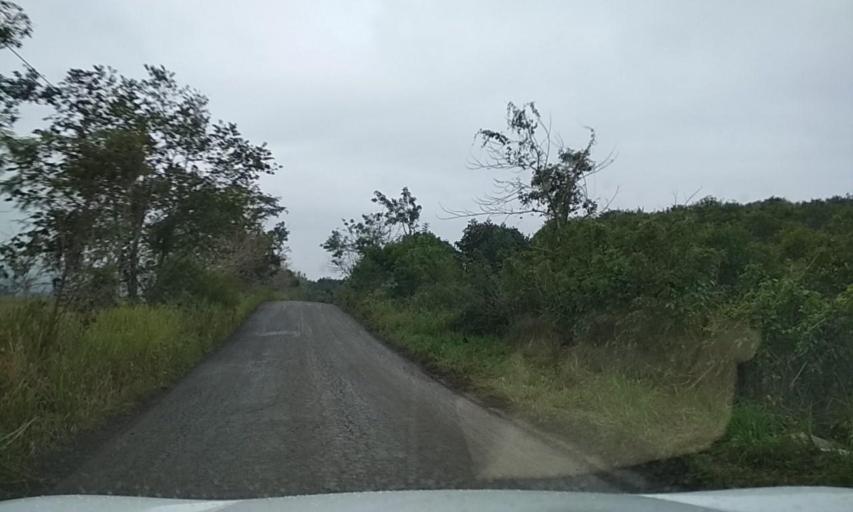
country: MX
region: Veracruz
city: Coatzintla
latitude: 20.4667
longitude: -97.4706
